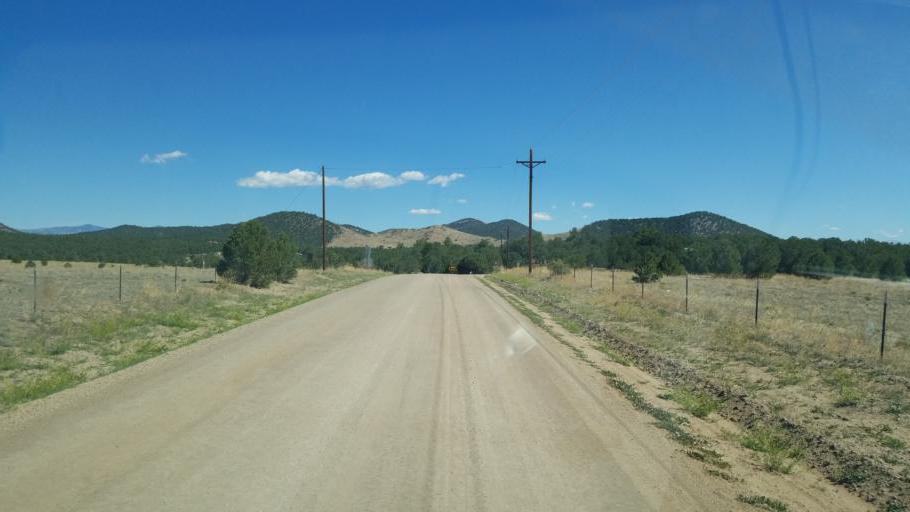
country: US
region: Colorado
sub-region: Custer County
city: Westcliffe
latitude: 38.2834
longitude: -105.5008
